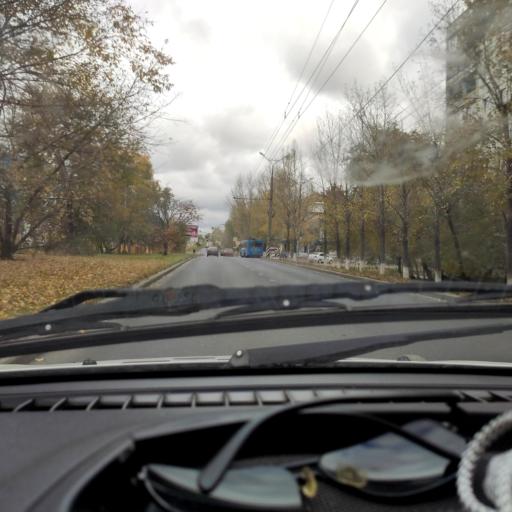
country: RU
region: Samara
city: Zhigulevsk
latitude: 53.4800
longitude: 49.4741
